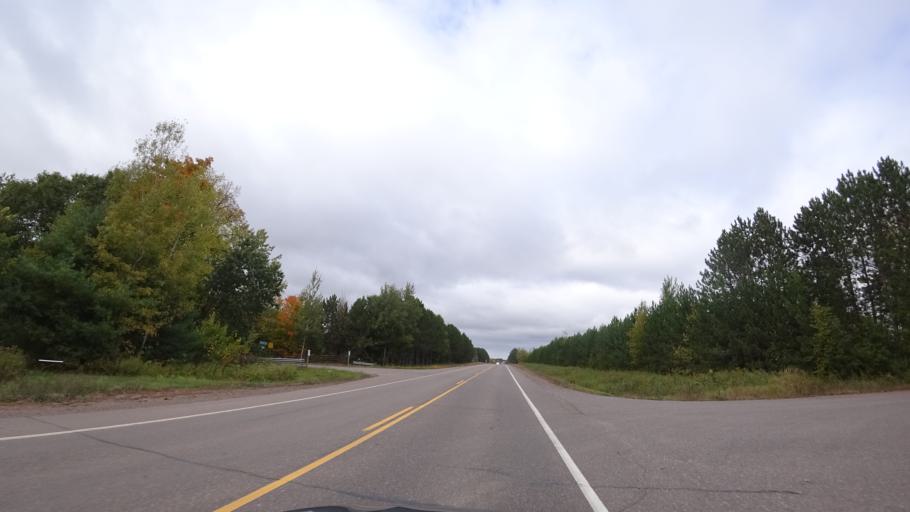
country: US
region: Wisconsin
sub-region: Rusk County
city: Ladysmith
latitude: 45.5167
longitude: -91.1115
